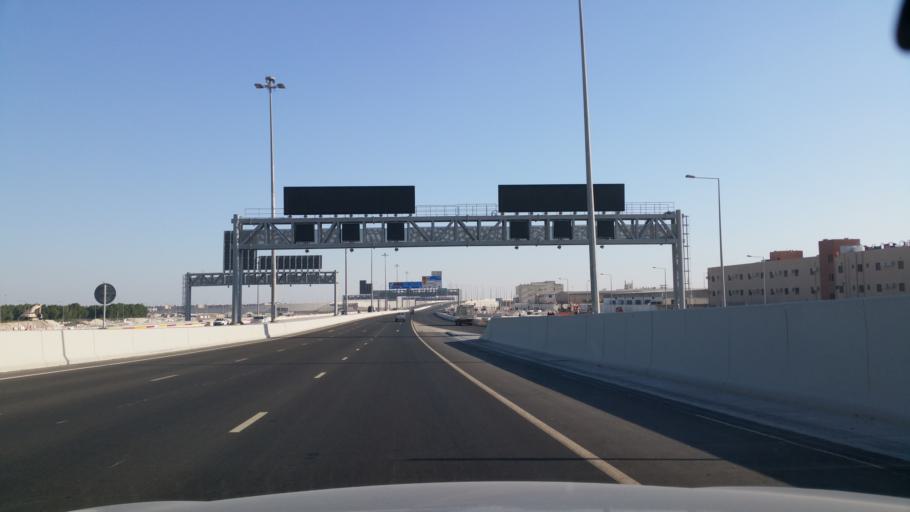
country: QA
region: Al Wakrah
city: Al Wukayr
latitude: 25.1758
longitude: 51.4675
